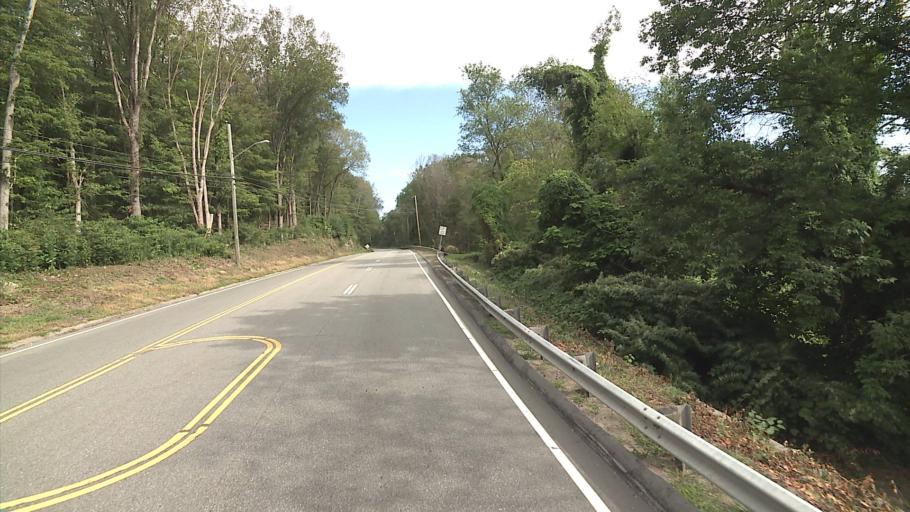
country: US
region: Connecticut
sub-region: New London County
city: Baltic
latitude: 41.6116
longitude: -72.1450
